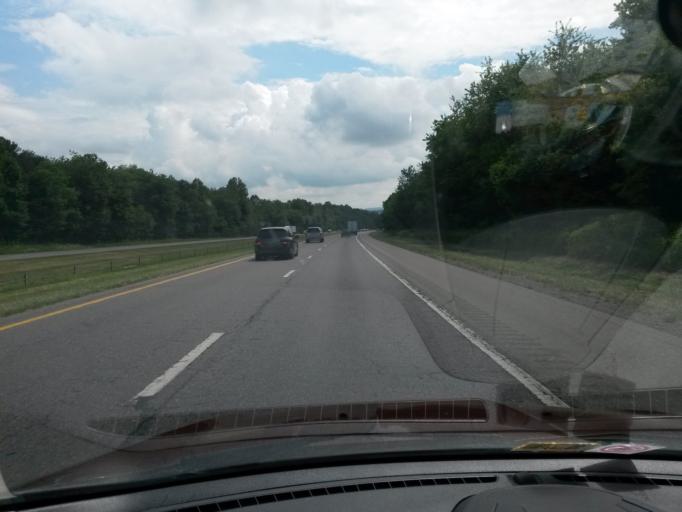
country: US
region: North Carolina
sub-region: Surry County
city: Elkin
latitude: 36.3230
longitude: -80.7965
